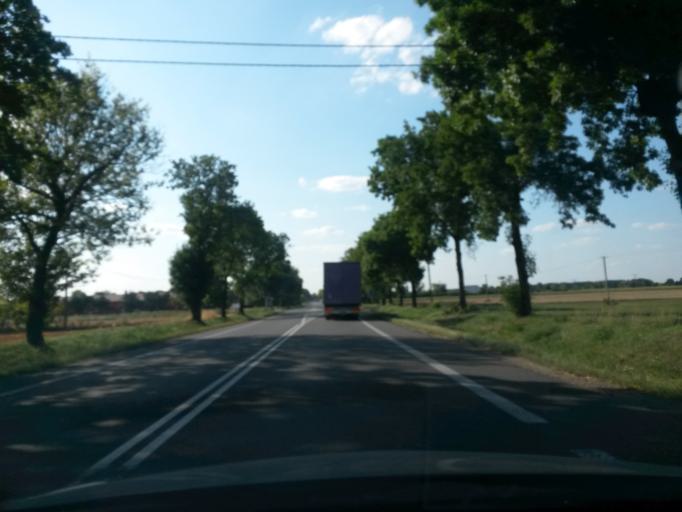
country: PL
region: Masovian Voivodeship
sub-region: Powiat sierpecki
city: Sierpc
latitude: 52.8410
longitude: 19.7268
